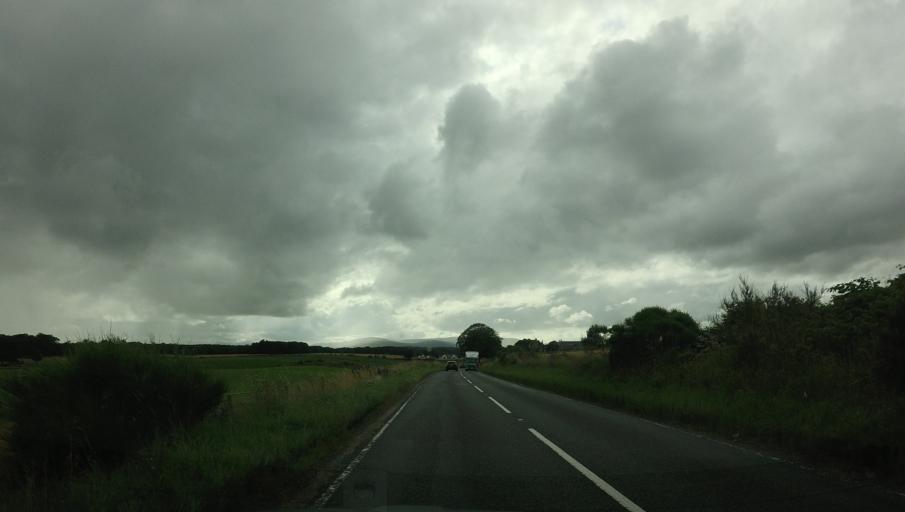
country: GB
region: Scotland
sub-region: Aberdeenshire
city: Westhill
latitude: 57.1421
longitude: -2.3148
